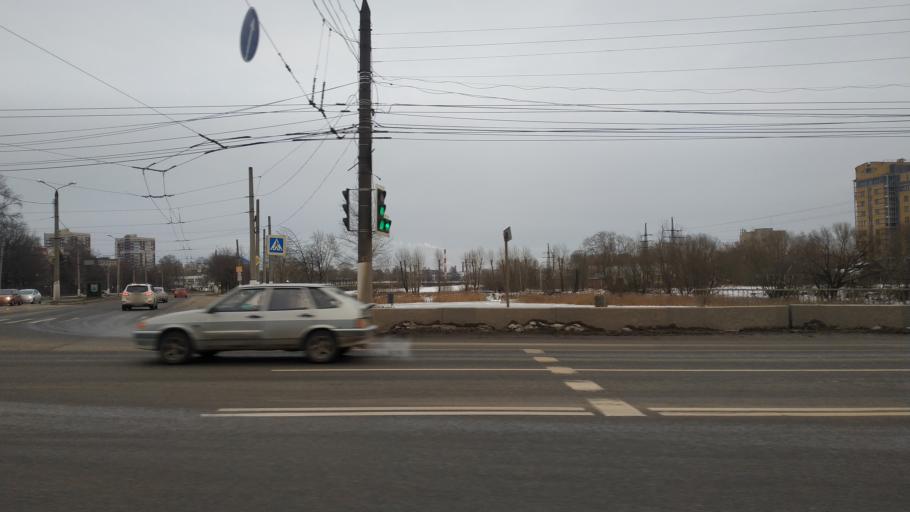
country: RU
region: Tverskaya
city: Tver
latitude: 56.8494
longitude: 35.9230
